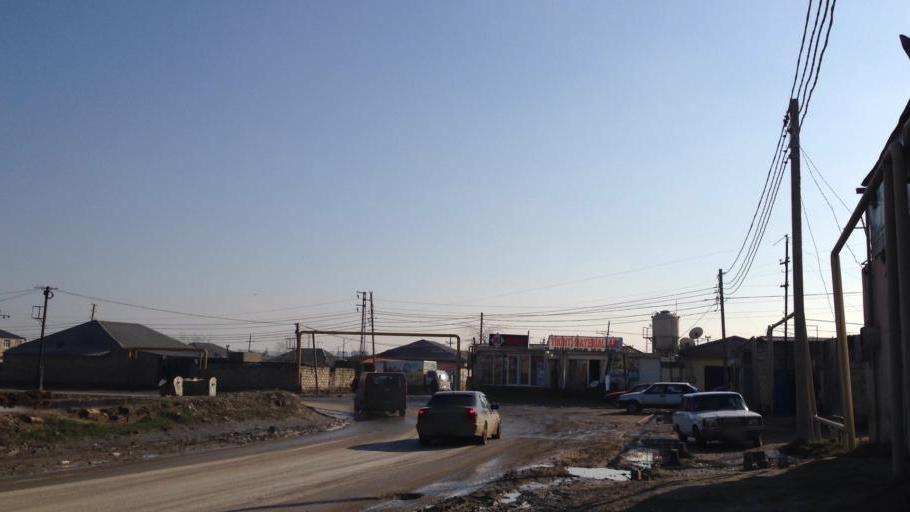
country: AZ
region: Baki
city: Sabuncu
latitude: 40.4488
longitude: 49.9315
